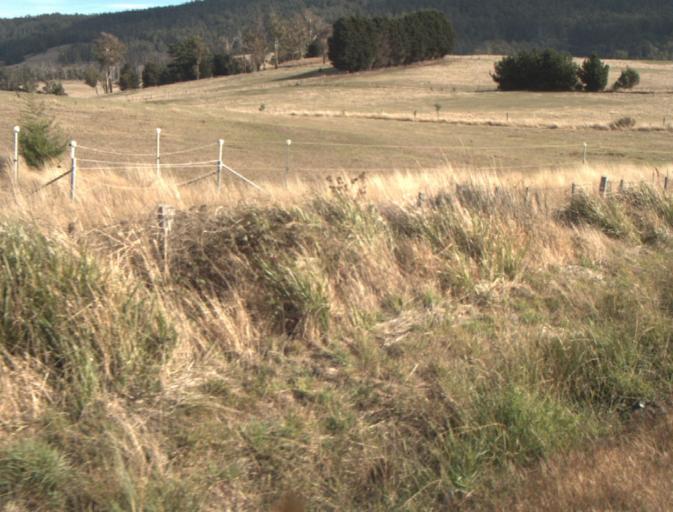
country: AU
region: Tasmania
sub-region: Launceston
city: Mayfield
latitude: -41.2086
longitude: 147.1160
